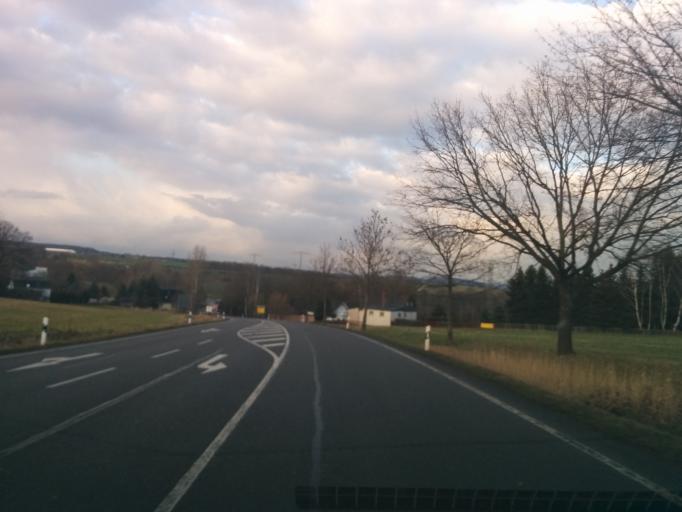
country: DE
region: Saxony
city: Niederwiesa
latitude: 50.8845
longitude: 12.9873
